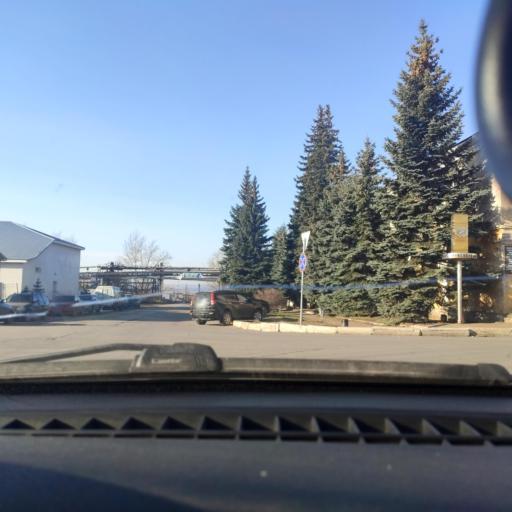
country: RU
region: Bashkortostan
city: Ufa
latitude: 54.8392
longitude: 56.0889
